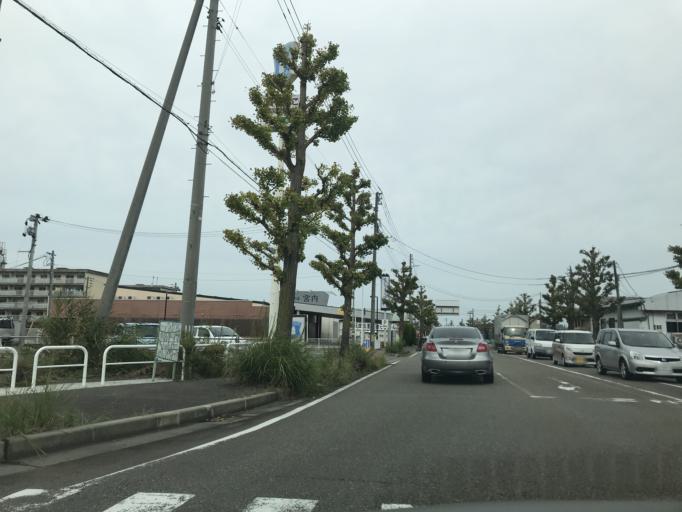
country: JP
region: Niigata
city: Nagaoka
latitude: 37.4273
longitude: 138.8358
